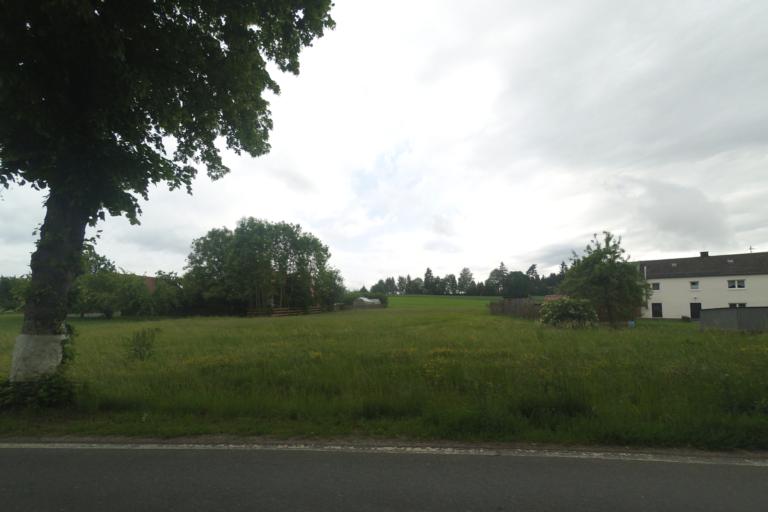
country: DE
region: Bavaria
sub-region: Upper Franconia
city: Sparneck
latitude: 50.1605
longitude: 11.8206
